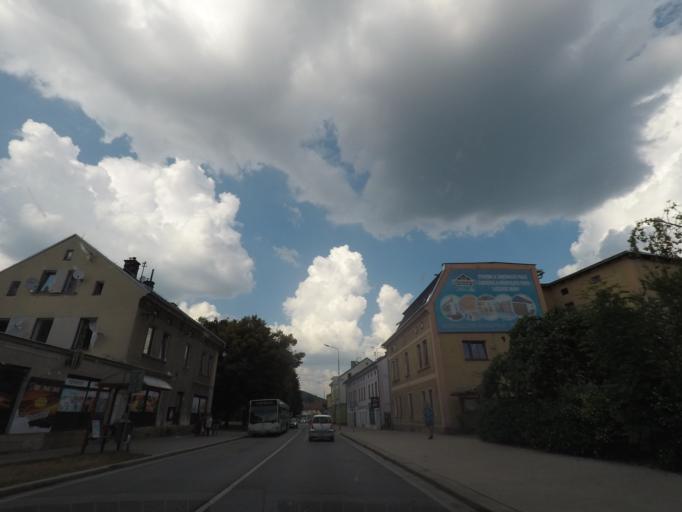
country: CZ
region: Kralovehradecky
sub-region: Okres Trutnov
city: Trutnov
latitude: 50.5731
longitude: 15.9490
